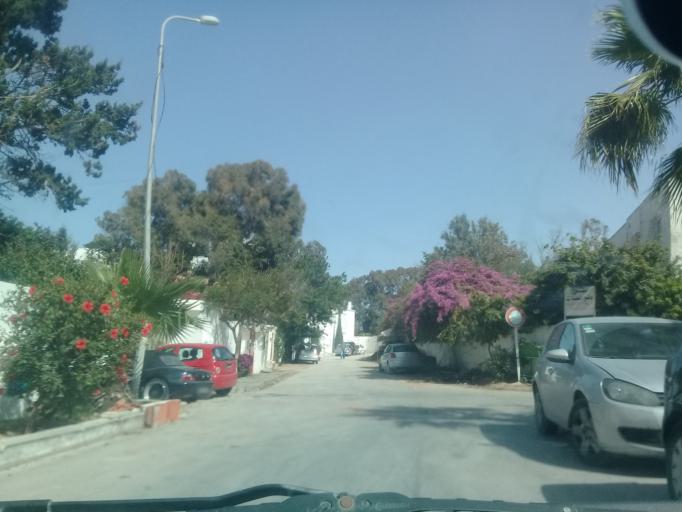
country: TN
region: Tunis
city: Al Marsa
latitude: 36.8879
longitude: 10.3282
